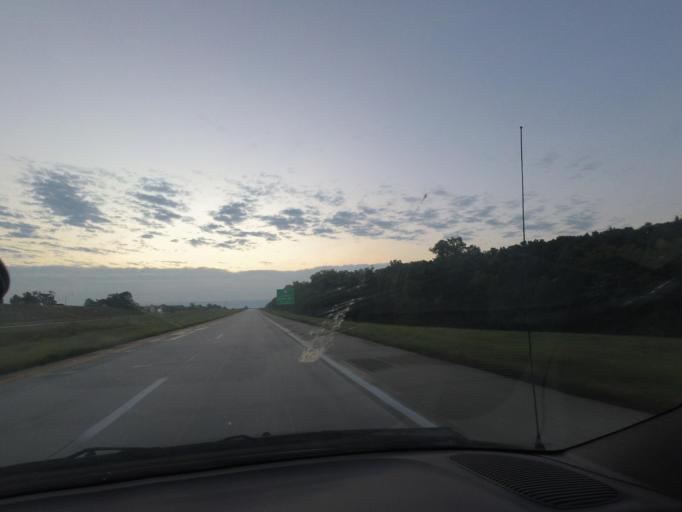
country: US
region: Missouri
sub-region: Macon County
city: Macon
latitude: 39.7586
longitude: -92.6510
